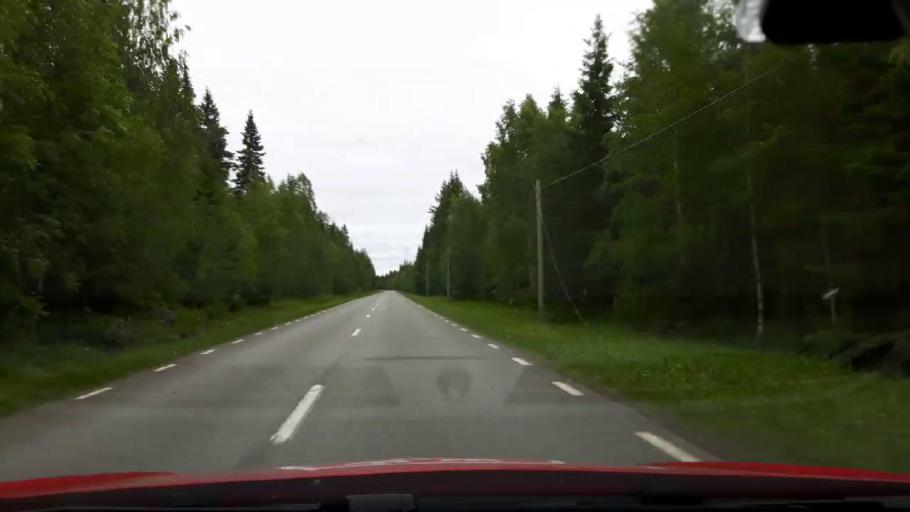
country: SE
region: Jaemtland
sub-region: Stroemsunds Kommun
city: Stroemsund
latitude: 63.4042
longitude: 15.6238
